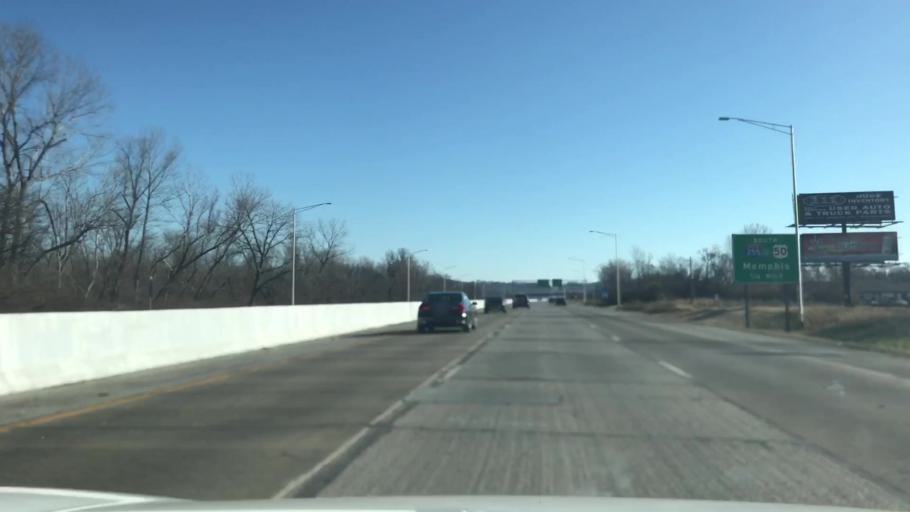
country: US
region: Illinois
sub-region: Saint Clair County
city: Alorton
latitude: 38.5891
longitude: -90.1154
